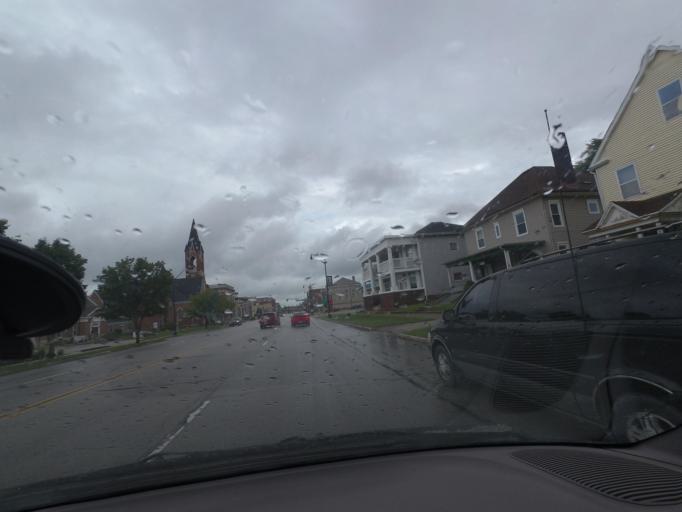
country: US
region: Indiana
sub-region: Montgomery County
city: Crawfordsville
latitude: 40.0384
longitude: -86.9011
